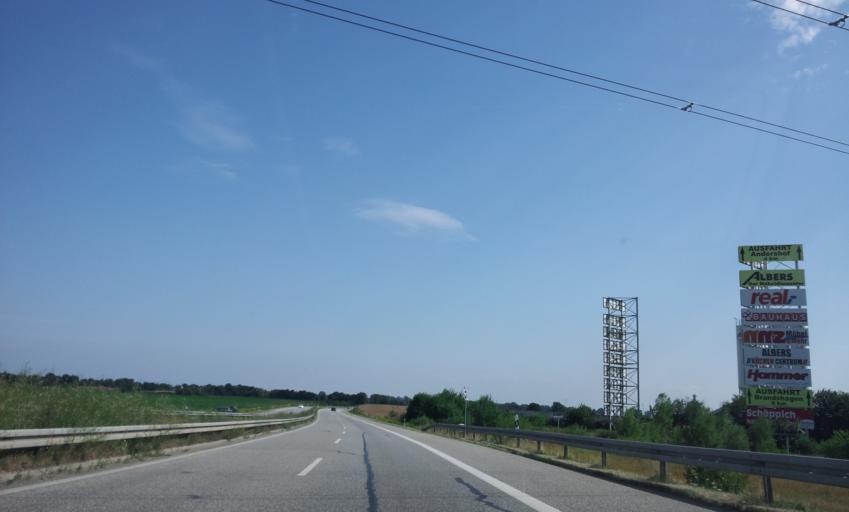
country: DE
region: Mecklenburg-Vorpommern
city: Wendorf
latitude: 54.2816
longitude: 13.0745
